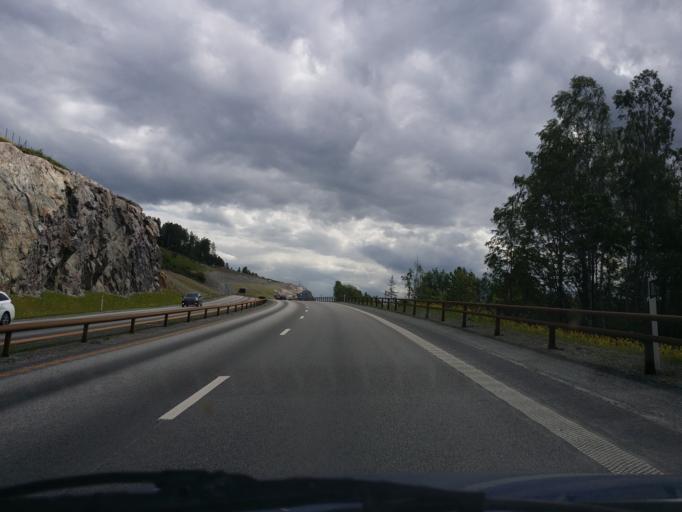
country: NO
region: Akershus
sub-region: Eidsvoll
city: Eidsvoll
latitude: 60.5021
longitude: 11.2387
